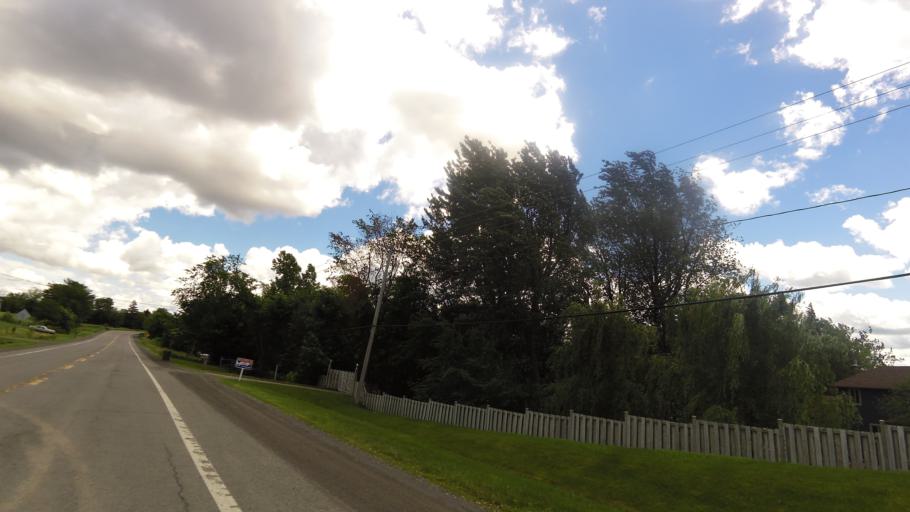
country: CA
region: Quebec
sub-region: Monteregie
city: Rigaud
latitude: 45.5306
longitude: -74.2359
